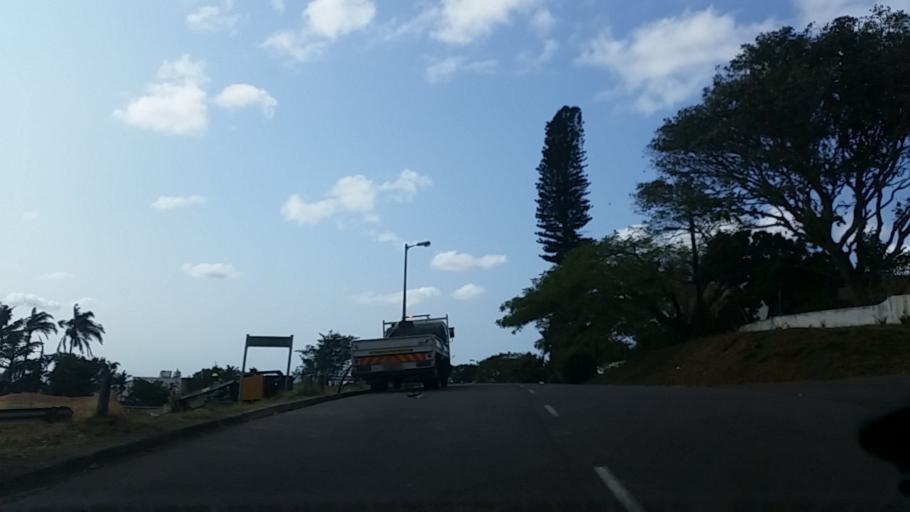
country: ZA
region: KwaZulu-Natal
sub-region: eThekwini Metropolitan Municipality
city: Berea
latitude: -29.8305
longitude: 30.9460
